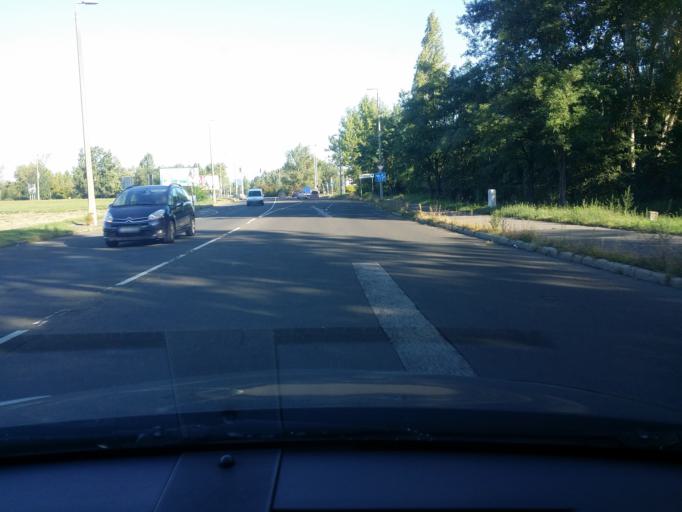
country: HU
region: Budapest
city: Budapest XV. keruelet
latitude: 47.5889
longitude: 19.1022
